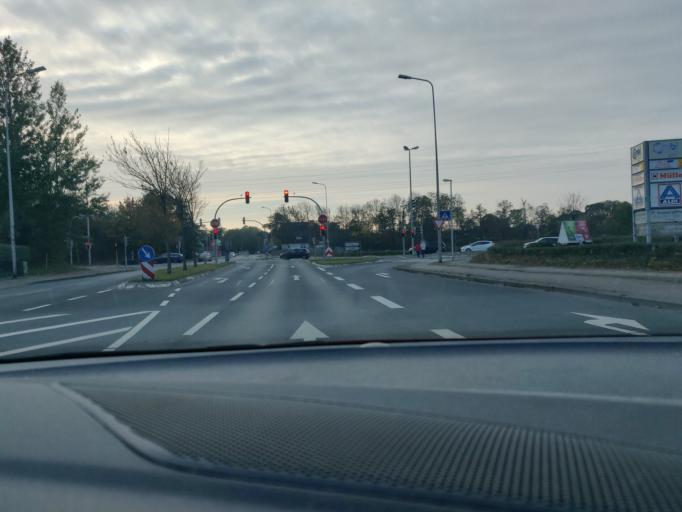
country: DE
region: Lower Saxony
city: Cuxhaven
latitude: 53.8598
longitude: 8.6738
